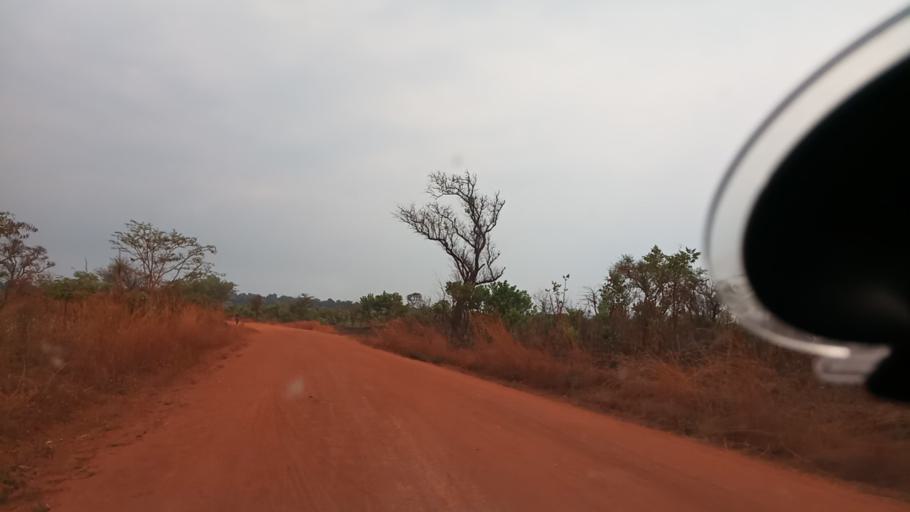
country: ZM
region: Luapula
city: Nchelenge
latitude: -9.1107
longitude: 28.3032
